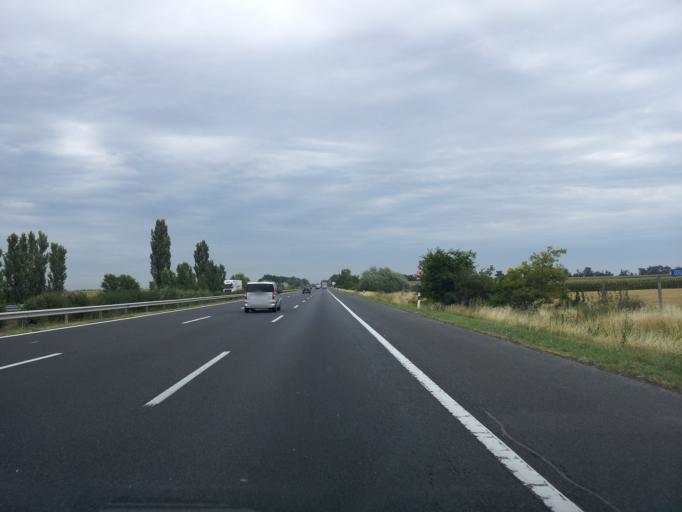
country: HU
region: Fejer
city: Kapolnasnyek
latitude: 47.2643
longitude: 18.6847
